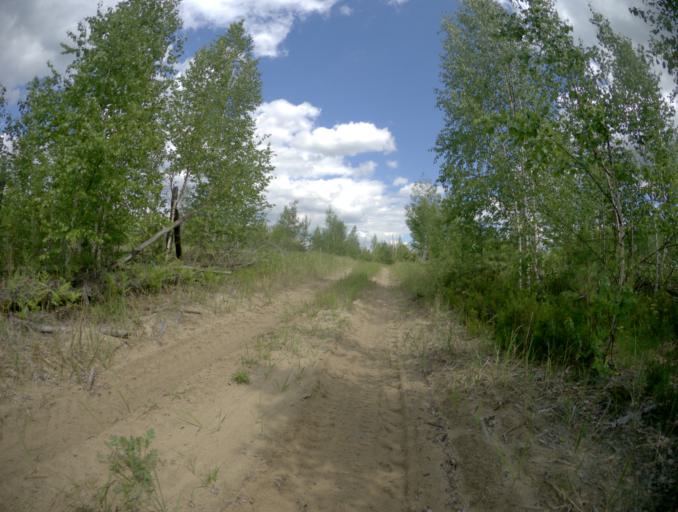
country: RU
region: Vladimir
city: Velikodvorskiy
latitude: 55.2712
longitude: 40.8620
